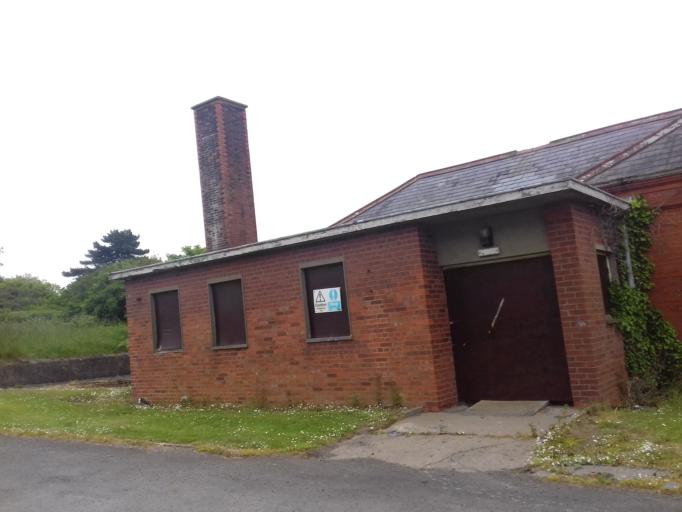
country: IE
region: Leinster
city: Portraine
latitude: 53.4848
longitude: -6.1095
